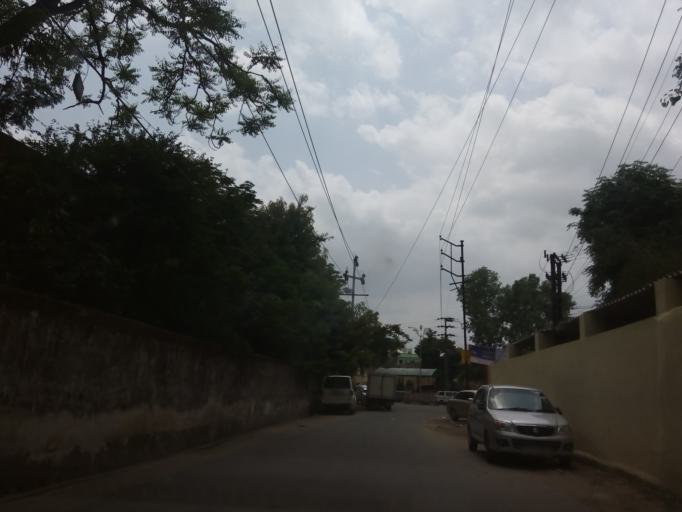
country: IN
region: Rajasthan
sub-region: Udaipur
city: Udaipur
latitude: 24.5780
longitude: 73.6933
